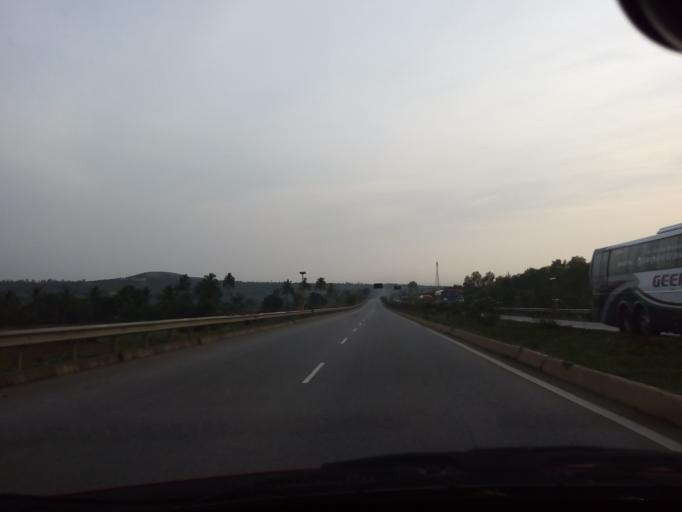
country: IN
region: Karnataka
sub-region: Chikkaballapur
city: Chik Ballapur
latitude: 13.5343
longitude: 77.7666
